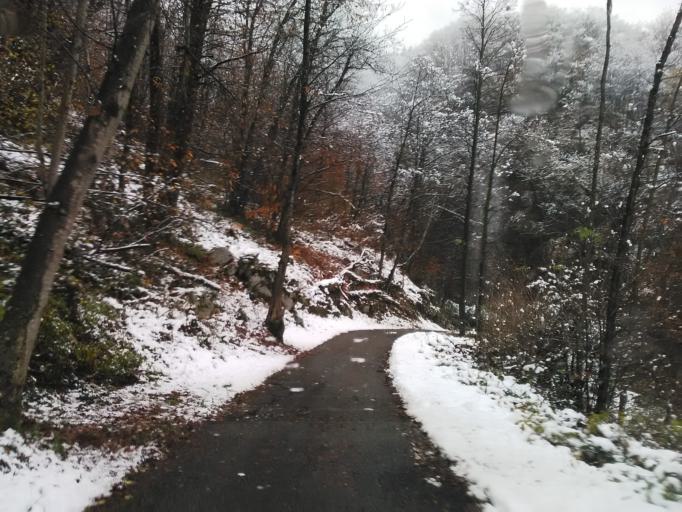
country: IT
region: Piedmont
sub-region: Provincia di Vercelli
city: Varallo
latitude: 45.7920
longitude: 8.2522
